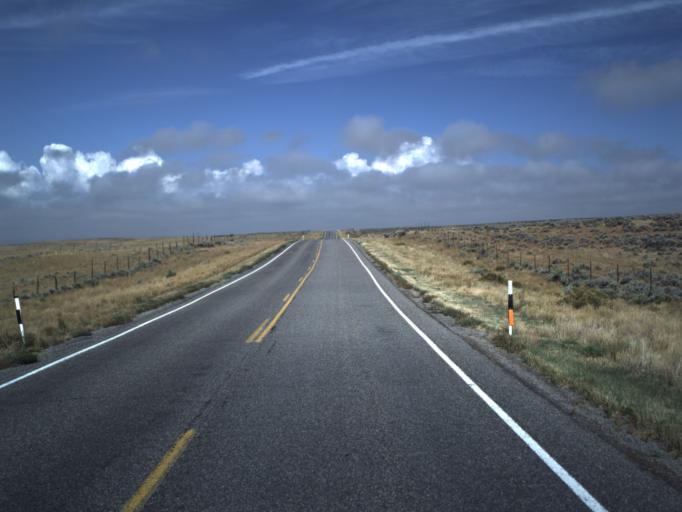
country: US
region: Wyoming
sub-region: Uinta County
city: Evanston
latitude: 41.4328
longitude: -111.0632
